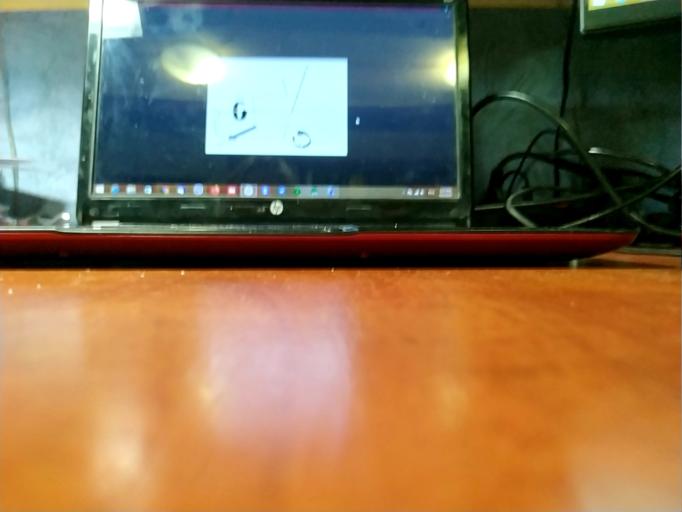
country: RU
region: Tverskaya
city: Sandovo
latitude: 58.6147
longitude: 36.4199
